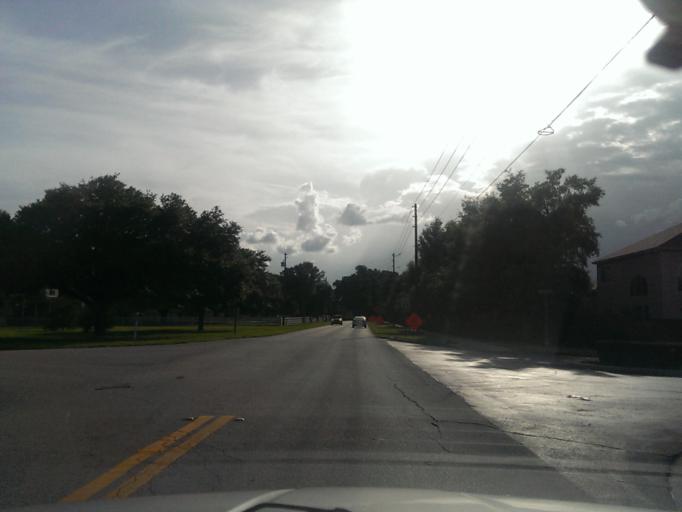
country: US
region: Florida
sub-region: Orange County
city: Winter Garden
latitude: 28.5370
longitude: -81.5706
